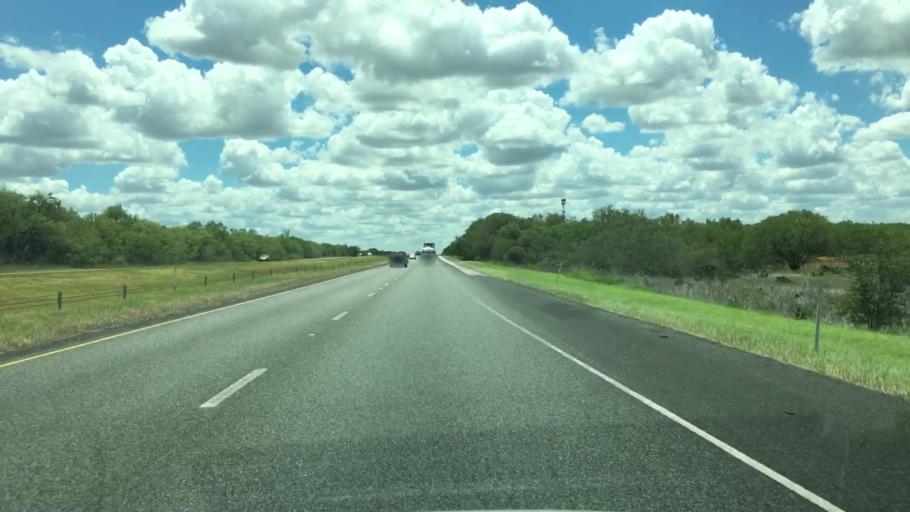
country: US
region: Texas
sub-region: Bexar County
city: Elmendorf
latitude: 29.1369
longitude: -98.4296
